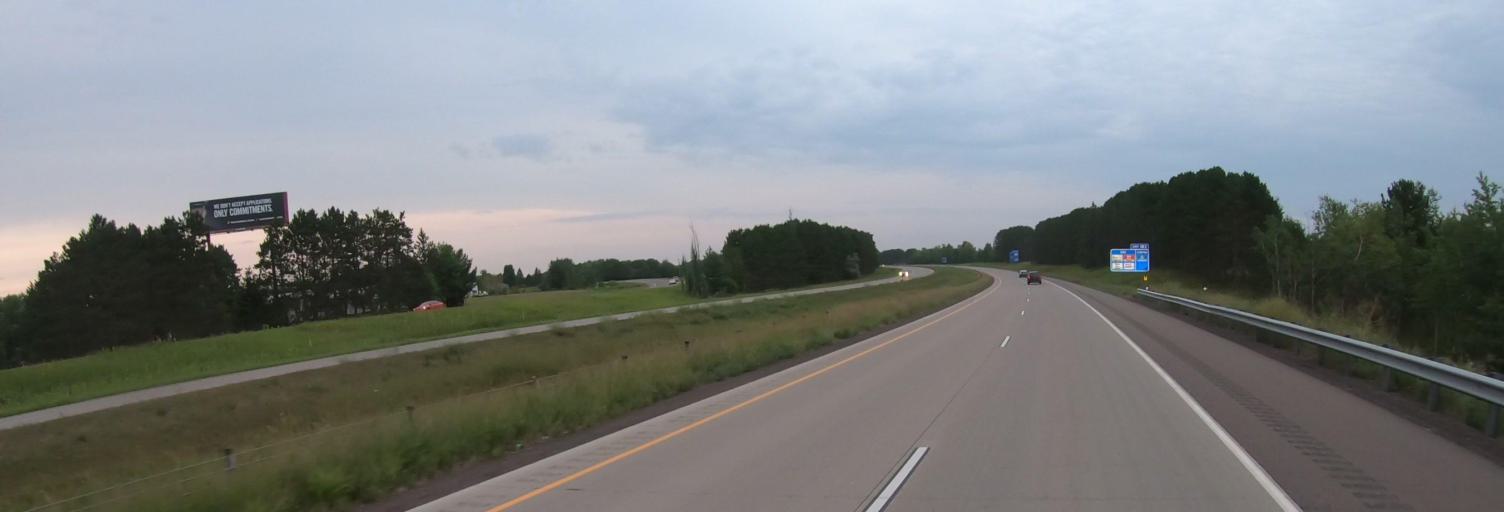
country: US
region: Minnesota
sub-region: Pine County
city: Hinckley
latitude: 45.9874
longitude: -92.9451
